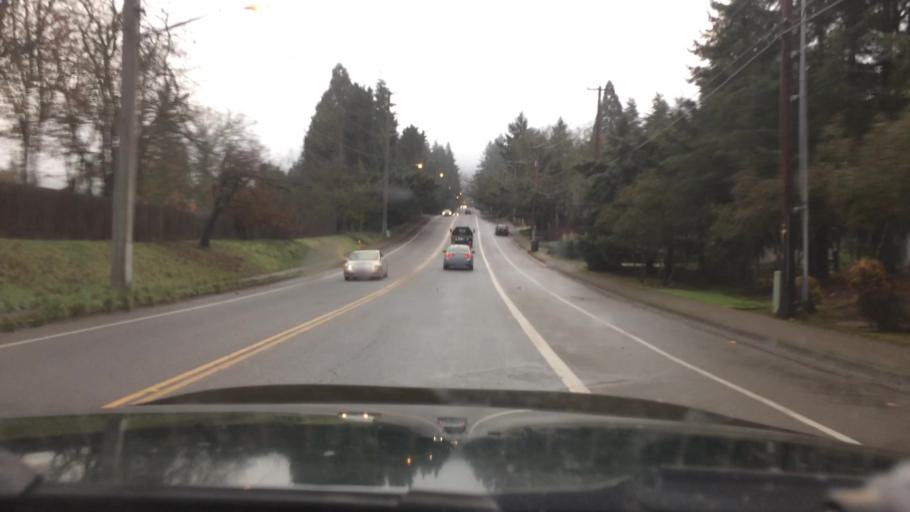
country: US
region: Oregon
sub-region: Lane County
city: Eugene
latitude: 44.0317
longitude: -123.1178
